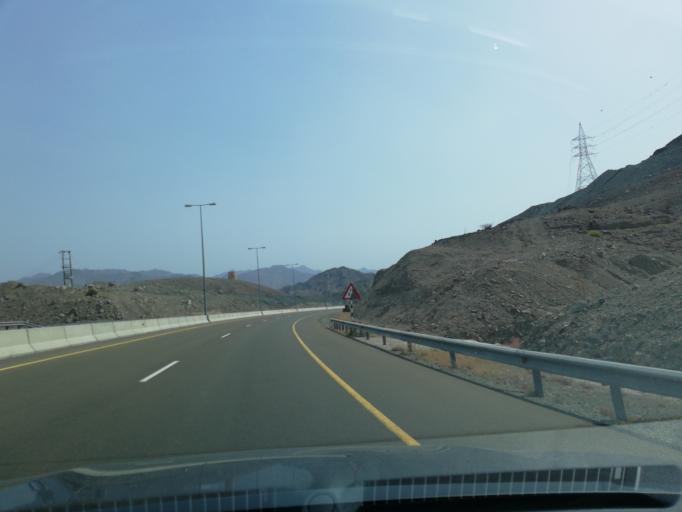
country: OM
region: Al Batinah
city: Al Liwa'
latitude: 24.2453
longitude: 56.3537
